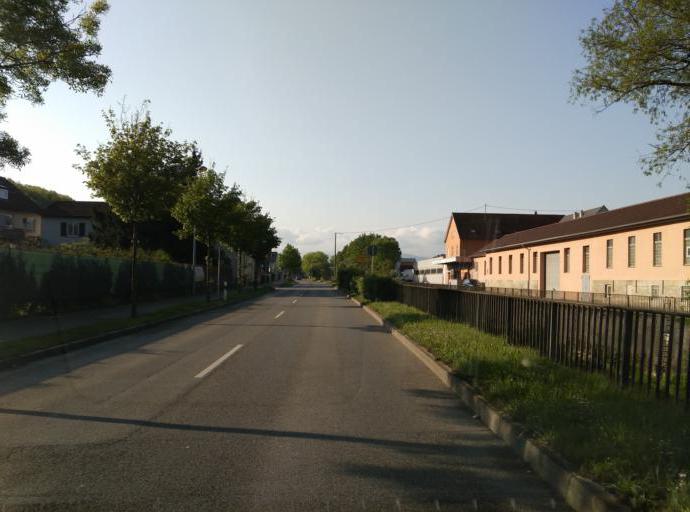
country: DE
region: Baden-Wuerttemberg
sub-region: Tuebingen Region
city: Wannweil
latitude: 48.5219
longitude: 9.1455
